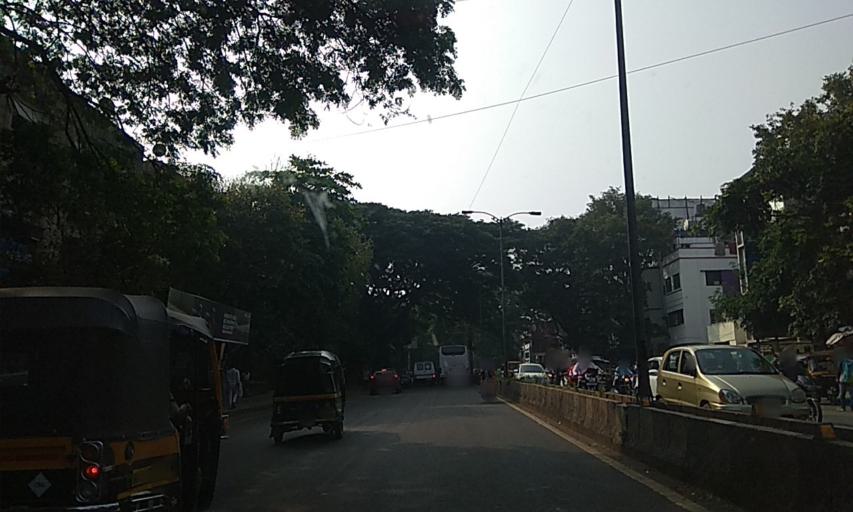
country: IN
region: Maharashtra
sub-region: Pune Division
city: Pune
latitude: 18.5059
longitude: 73.8447
